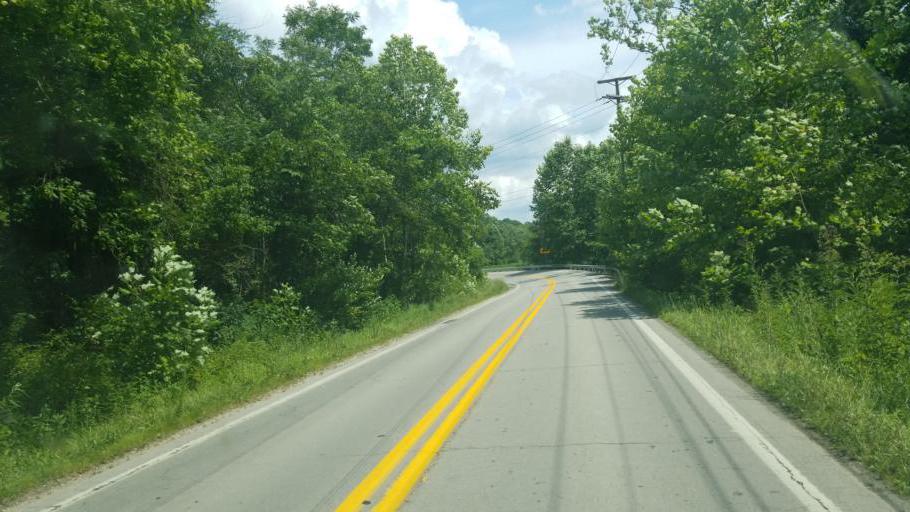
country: US
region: West Virginia
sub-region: Putnam County
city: Teays Valley
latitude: 38.4521
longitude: -81.8799
